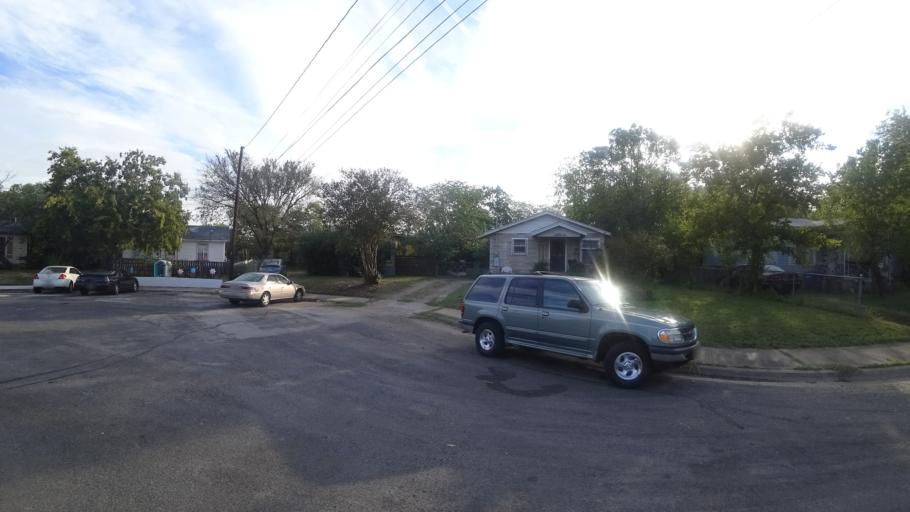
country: US
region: Texas
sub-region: Travis County
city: Austin
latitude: 30.2740
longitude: -97.7104
